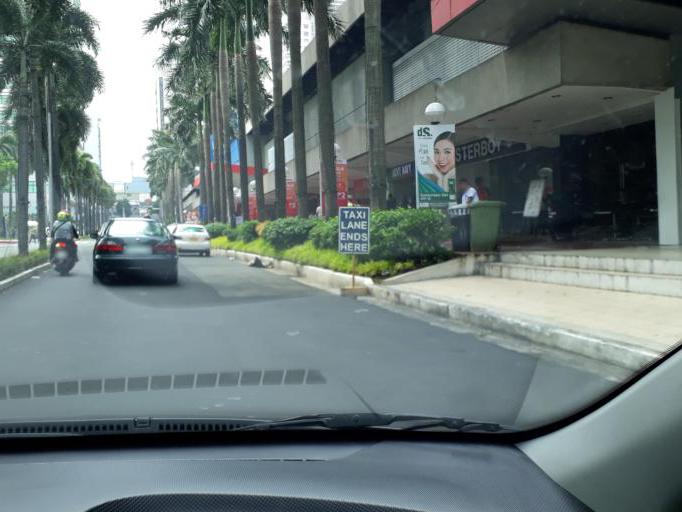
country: PH
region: Metro Manila
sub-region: Quezon City
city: Quezon City
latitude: 14.6202
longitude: 121.0545
